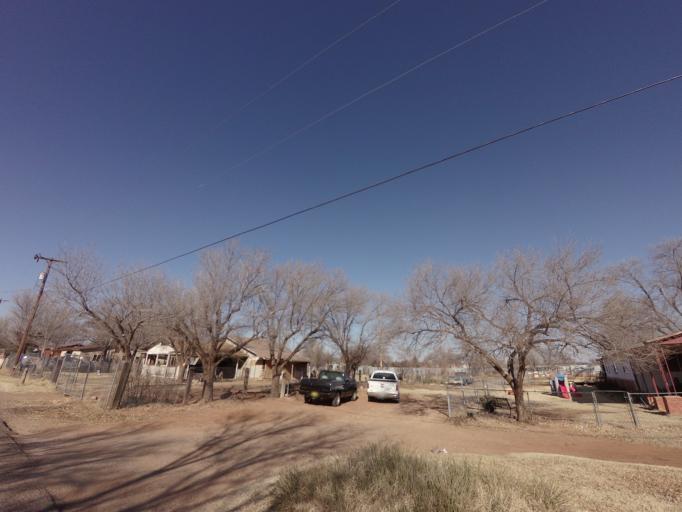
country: US
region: New Mexico
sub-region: Curry County
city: Clovis
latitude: 34.3864
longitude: -103.1821
